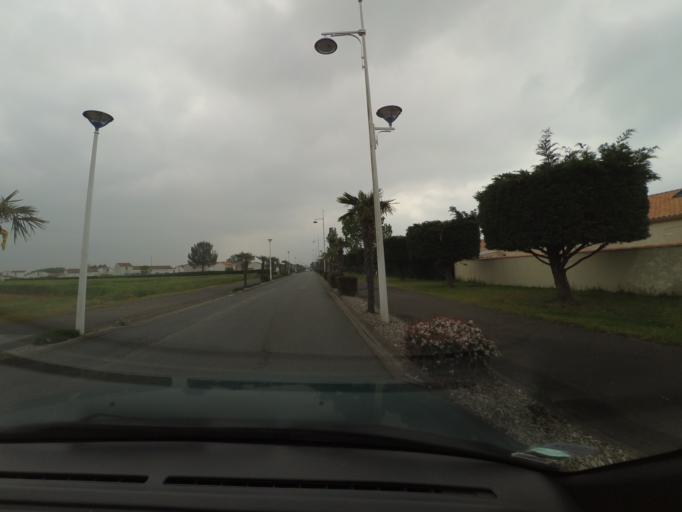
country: FR
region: Pays de la Loire
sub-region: Departement de la Vendee
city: Angles
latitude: 46.3398
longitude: -1.3383
